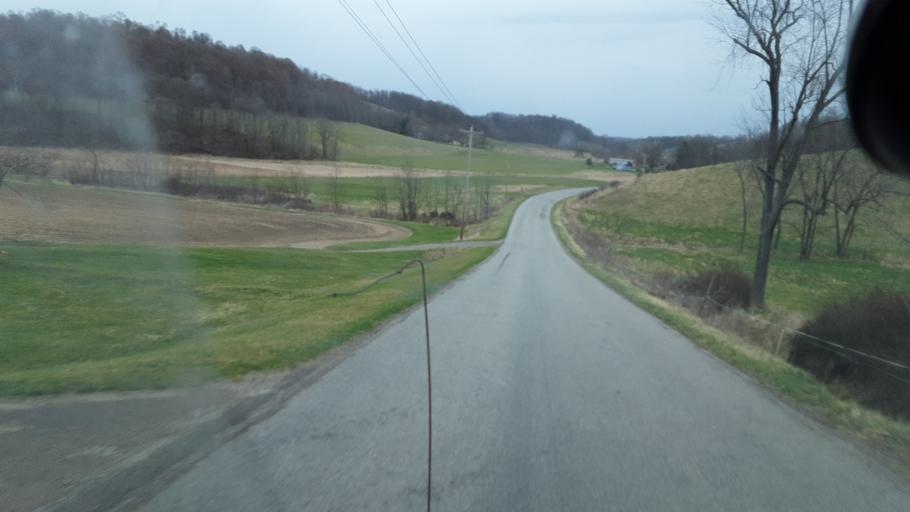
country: US
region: Ohio
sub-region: Coshocton County
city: West Lafayette
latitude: 40.3088
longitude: -81.7018
